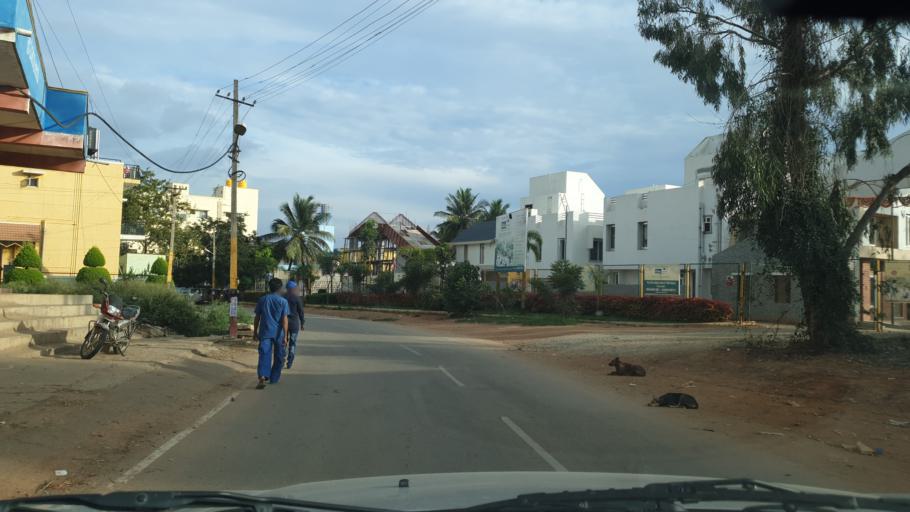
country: IN
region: Karnataka
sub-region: Bangalore Urban
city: Yelahanka
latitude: 13.1905
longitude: 77.6258
